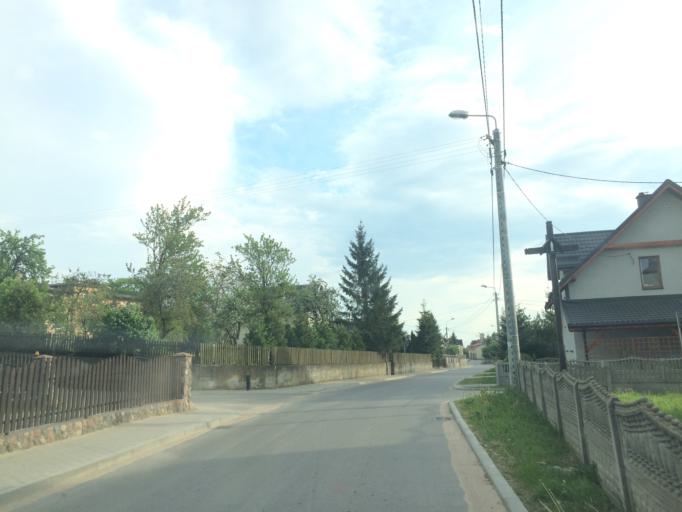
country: PL
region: Kujawsko-Pomorskie
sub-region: Powiat brodnicki
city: Brzozie
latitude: 53.3583
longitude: 19.7094
